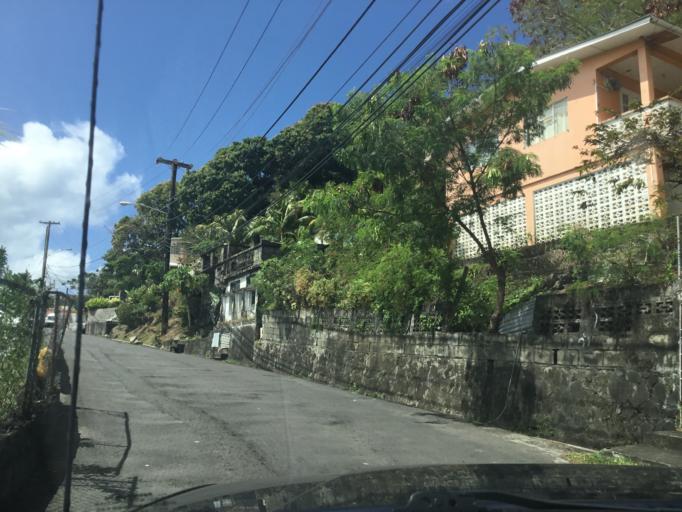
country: VC
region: Saint George
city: Kingstown Park
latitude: 13.1613
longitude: -61.2370
